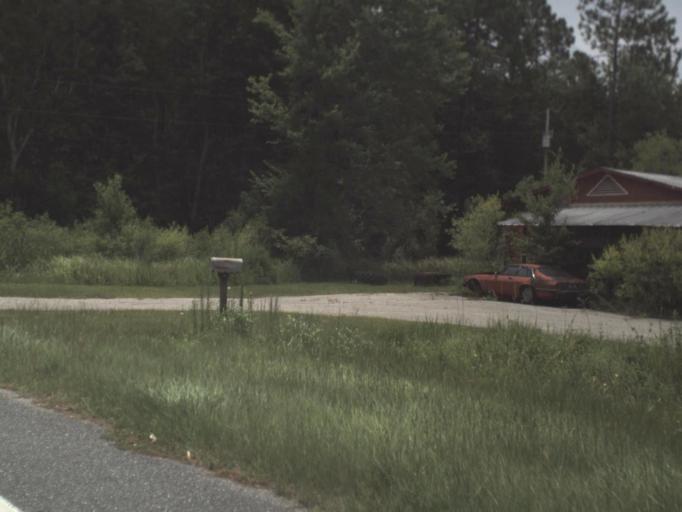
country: US
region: Florida
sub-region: Bradford County
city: Starke
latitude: 29.9453
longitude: -82.1363
